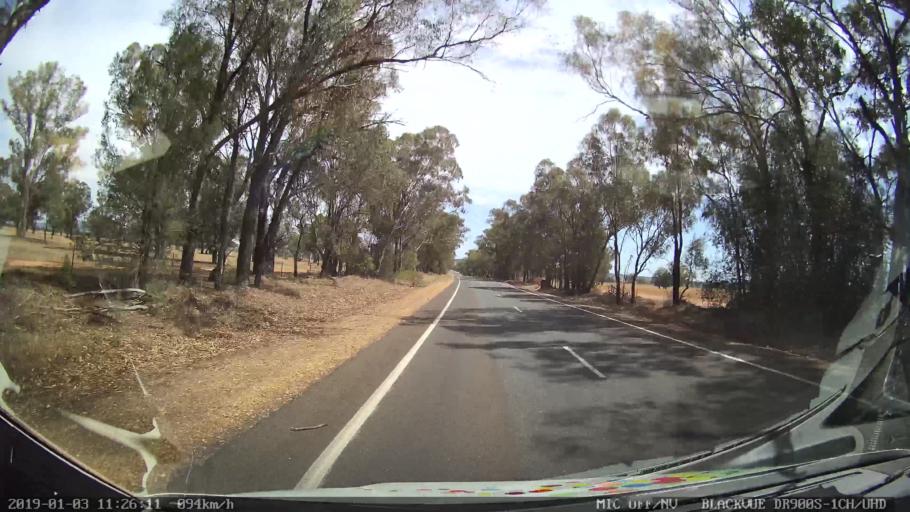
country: AU
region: New South Wales
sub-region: Weddin
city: Grenfell
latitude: -34.0284
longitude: 148.2266
